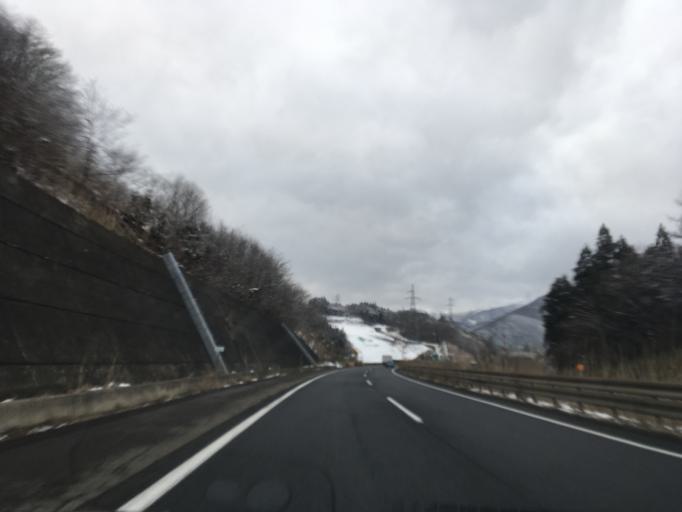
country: JP
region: Yamagata
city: Yamagata-shi
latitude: 38.2158
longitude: 140.5236
